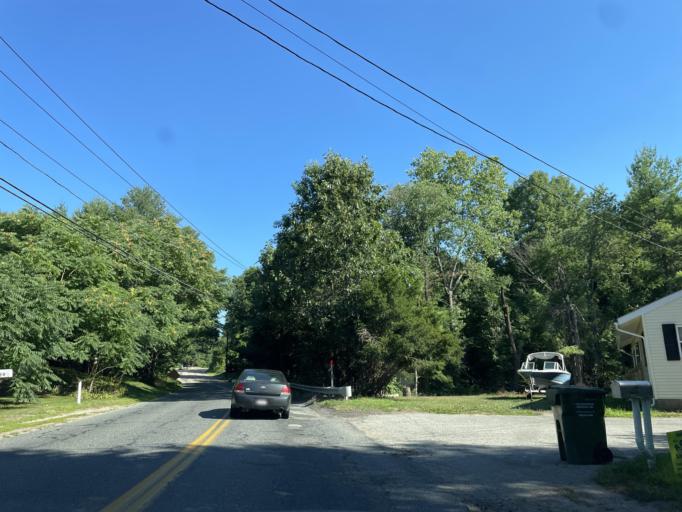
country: US
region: Massachusetts
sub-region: Worcester County
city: East Douglas
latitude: 42.0631
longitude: -71.6927
